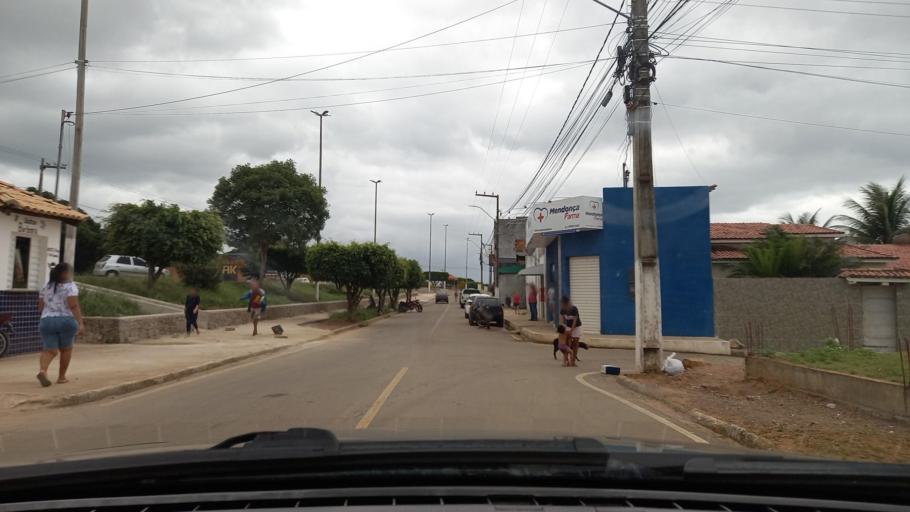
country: BR
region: Sergipe
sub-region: Caninde De Sao Francisco
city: Caninde de Sao Francisco
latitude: -9.6754
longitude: -37.7927
